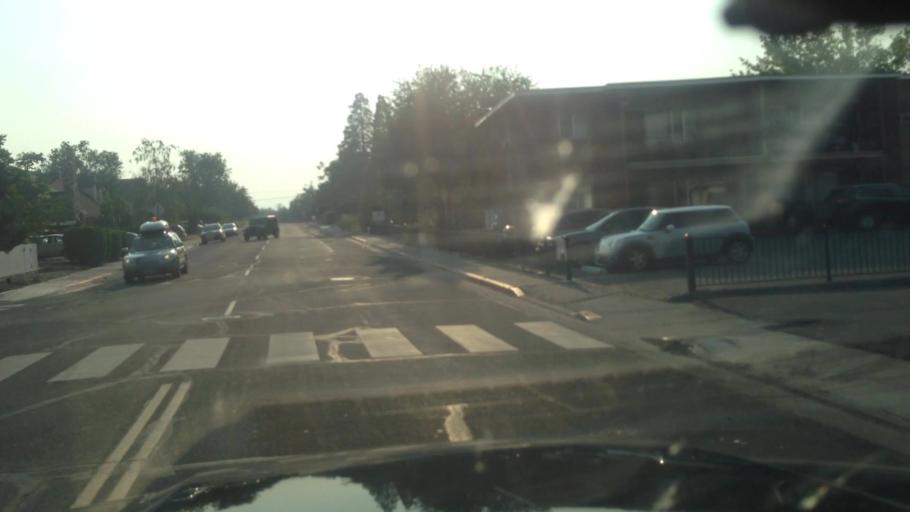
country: US
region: Nevada
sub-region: Washoe County
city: Reno
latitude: 39.5097
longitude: -119.8071
